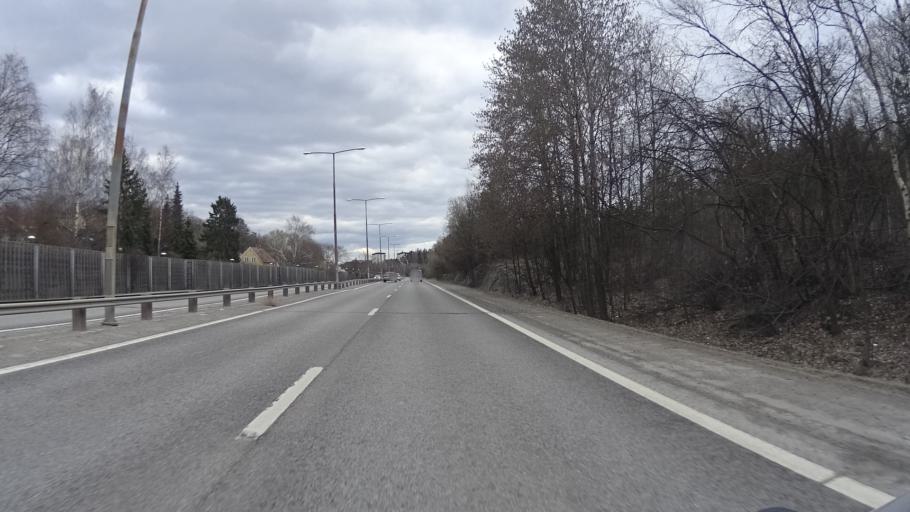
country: SE
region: Stockholm
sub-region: Stockholms Kommun
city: Arsta
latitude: 59.2684
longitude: 18.0198
